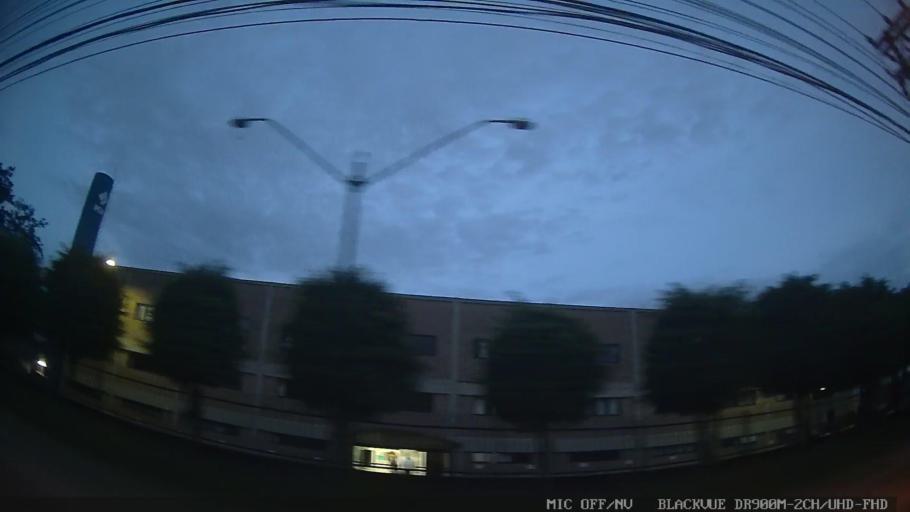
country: BR
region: Sao Paulo
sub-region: Itaquaquecetuba
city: Itaquaquecetuba
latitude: -23.4511
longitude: -46.3789
